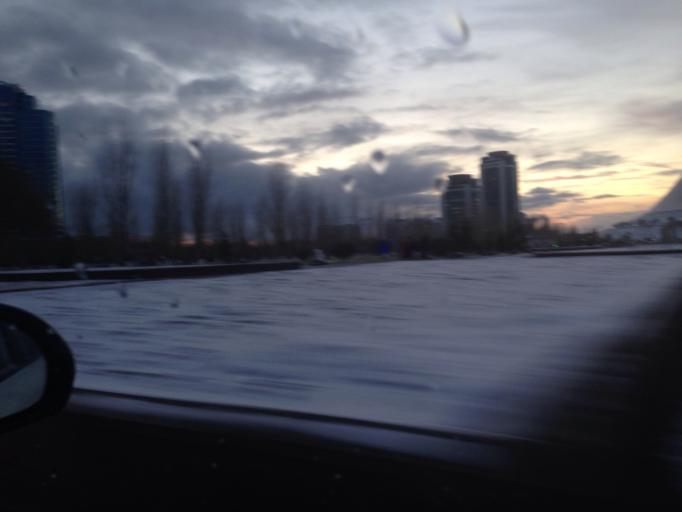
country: KZ
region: Astana Qalasy
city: Astana
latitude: 51.1314
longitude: 71.4114
